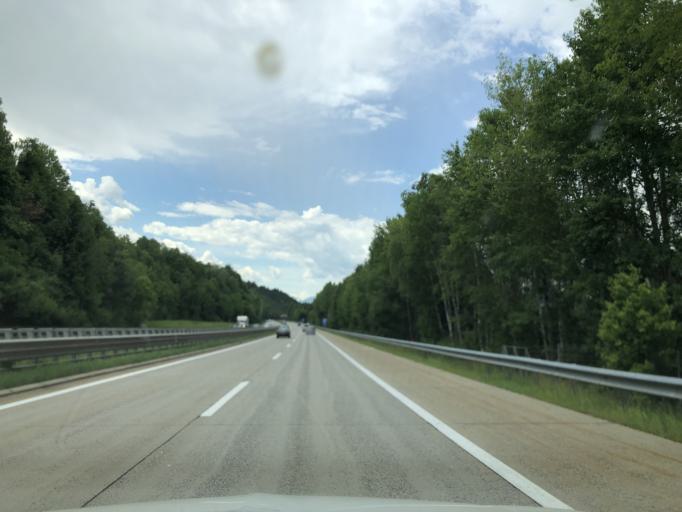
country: AT
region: Carinthia
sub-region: Politischer Bezirk Villach Land
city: Ferndorf
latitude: 46.7290
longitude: 13.6067
